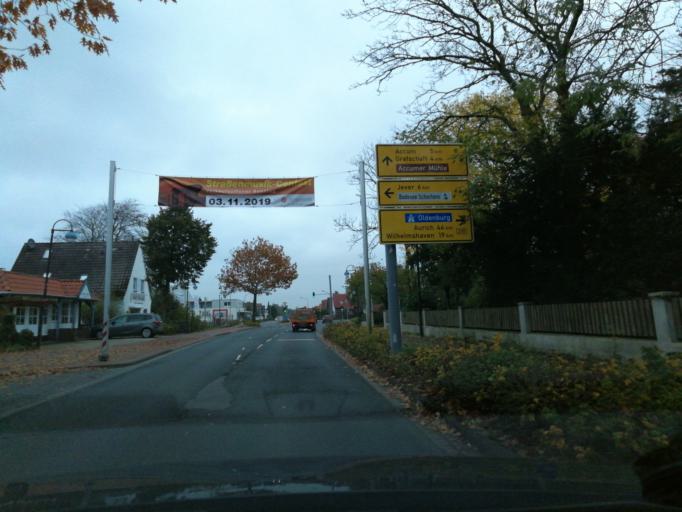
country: DE
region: Lower Saxony
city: Schortens
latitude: 53.5434
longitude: 7.9488
